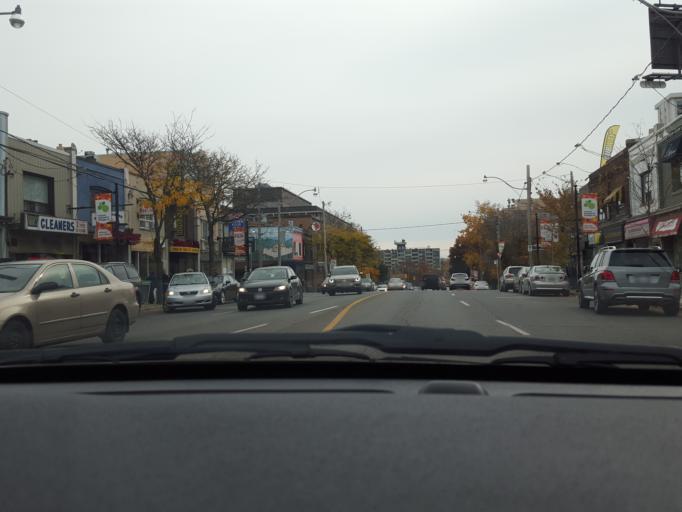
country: CA
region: Ontario
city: Toronto
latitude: 43.7021
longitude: -79.3877
